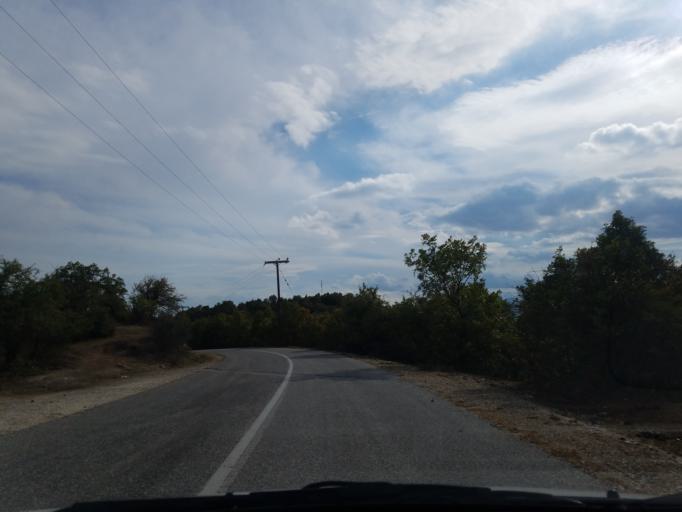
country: GR
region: Thessaly
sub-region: Trikala
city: Kastraki
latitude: 39.7344
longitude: 21.6550
